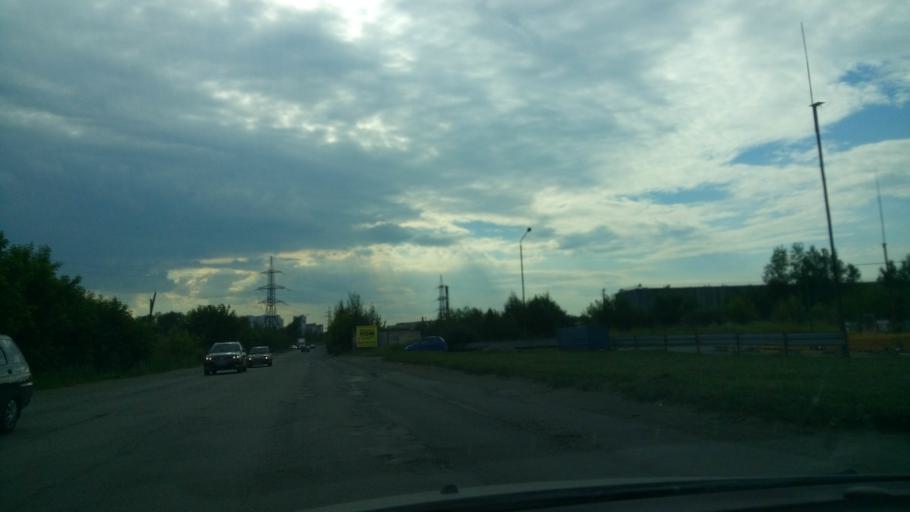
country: RU
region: Sverdlovsk
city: Yekaterinburg
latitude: 56.8874
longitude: 60.6676
